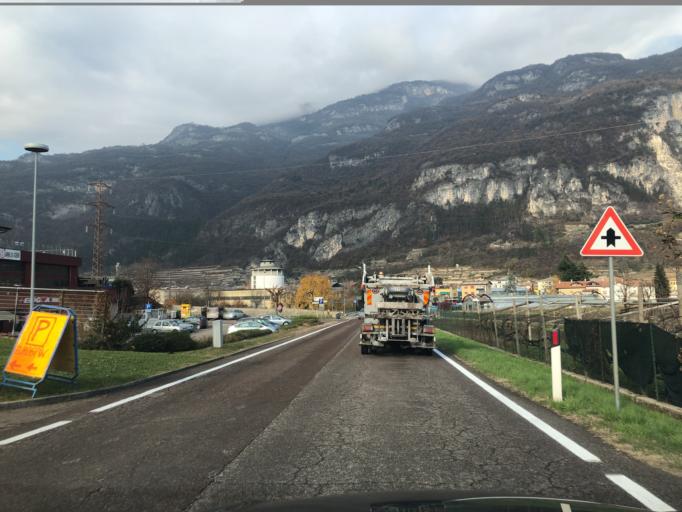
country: IT
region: Trentino-Alto Adige
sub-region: Provincia di Trento
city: Mori
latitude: 45.8483
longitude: 10.9745
